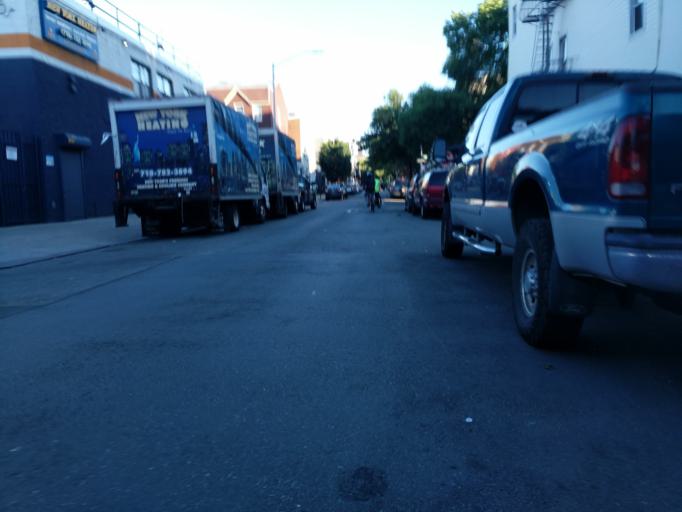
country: US
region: New York
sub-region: Queens County
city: Long Island City
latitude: 40.7144
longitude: -73.9426
